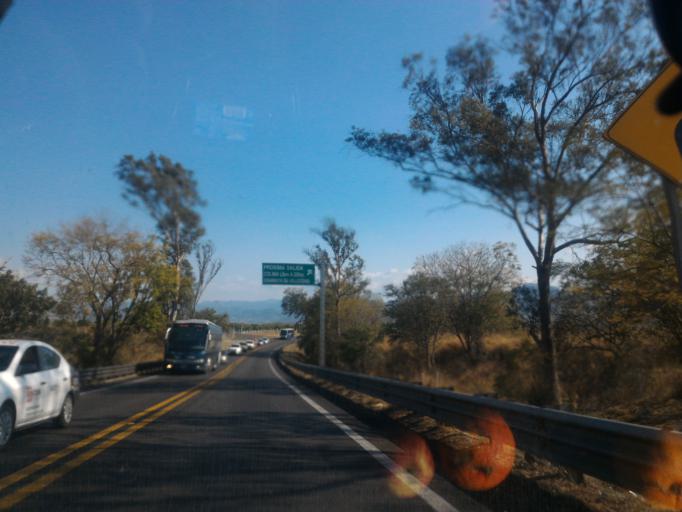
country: MX
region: Jalisco
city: Tuxpan
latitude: 19.5391
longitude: -103.4244
